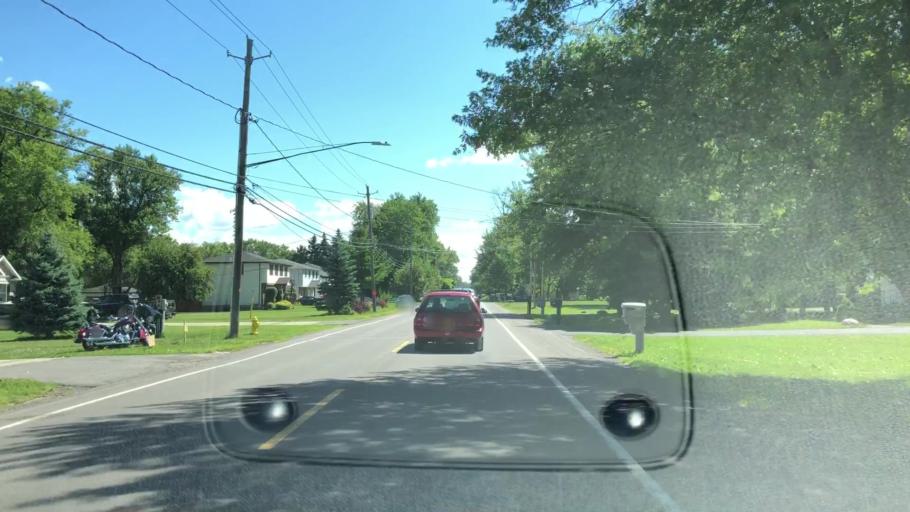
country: US
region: New York
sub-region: Erie County
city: Cheektowaga
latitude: 42.8509
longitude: -78.7350
